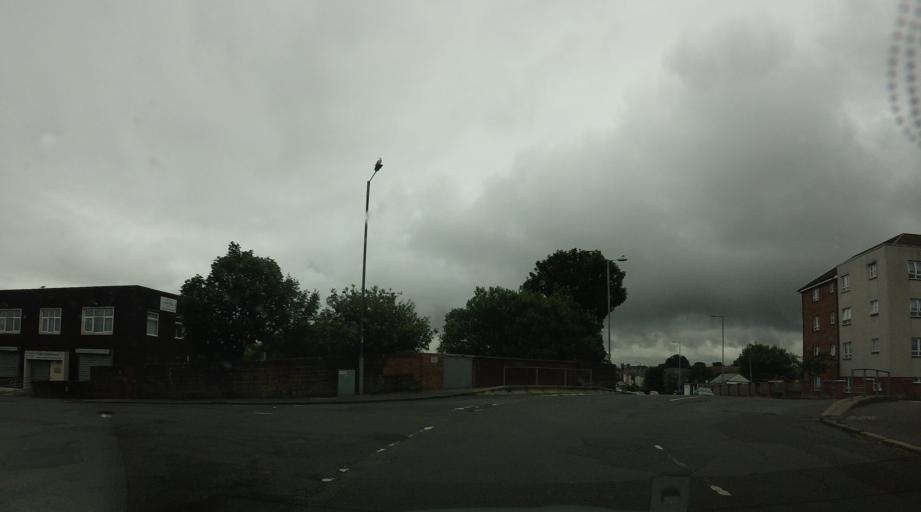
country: GB
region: Scotland
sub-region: South Ayrshire
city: Prestwick
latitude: 55.4719
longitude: -4.6176
